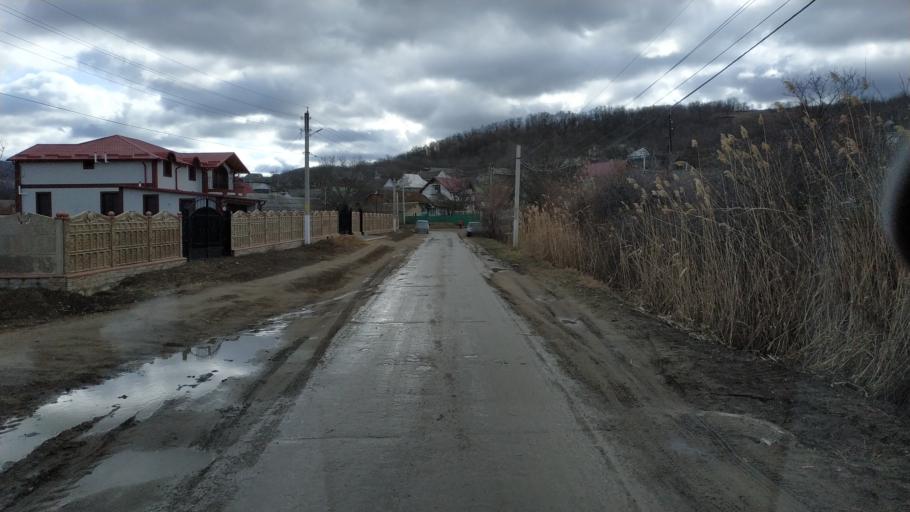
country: MD
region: Stinga Nistrului
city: Bucovat
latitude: 47.1335
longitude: 28.3813
